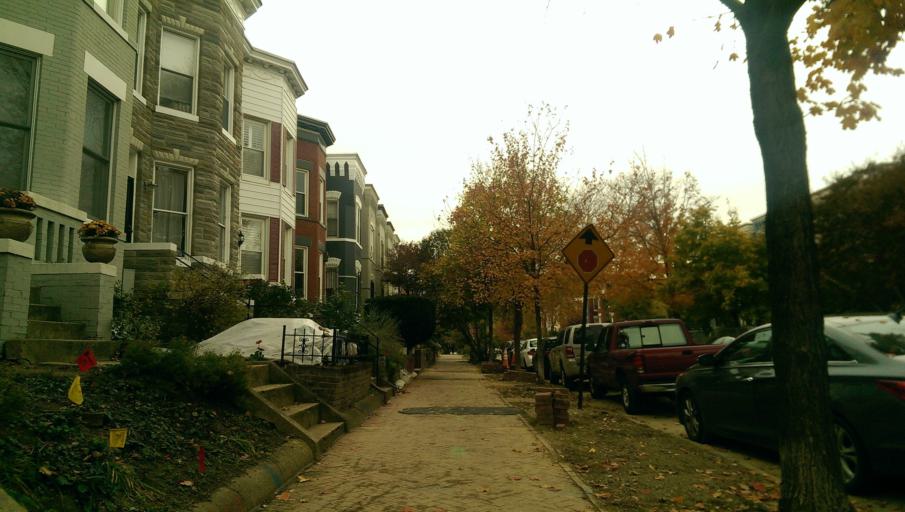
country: US
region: Washington, D.C.
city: Washington, D.C.
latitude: 38.8989
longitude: -76.9995
